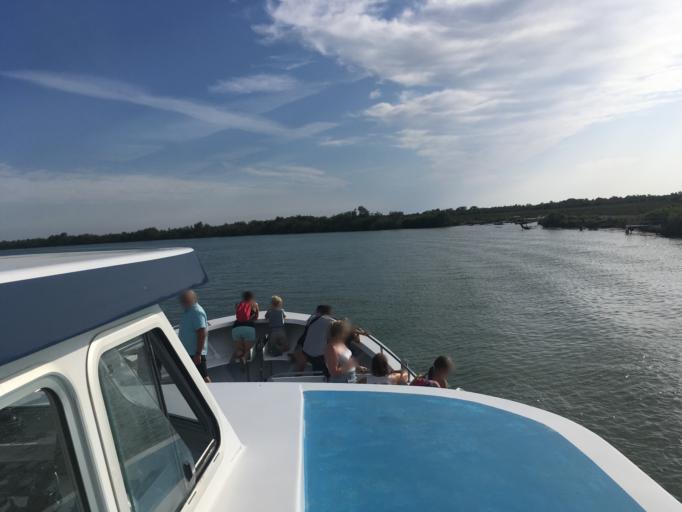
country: FR
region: Provence-Alpes-Cote d'Azur
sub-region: Departement des Bouches-du-Rhone
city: Saintes-Maries-de-la-Mer
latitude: 43.4761
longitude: 4.3884
